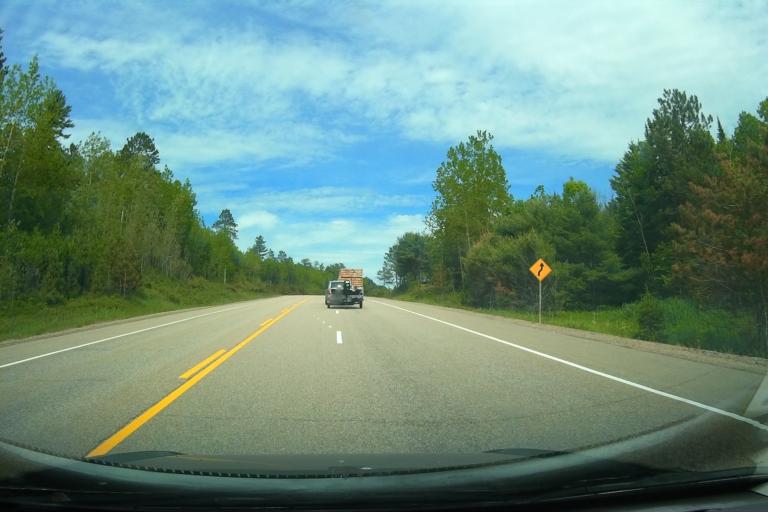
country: CA
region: Ontario
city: Mattawa
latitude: 46.2736
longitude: -78.9696
